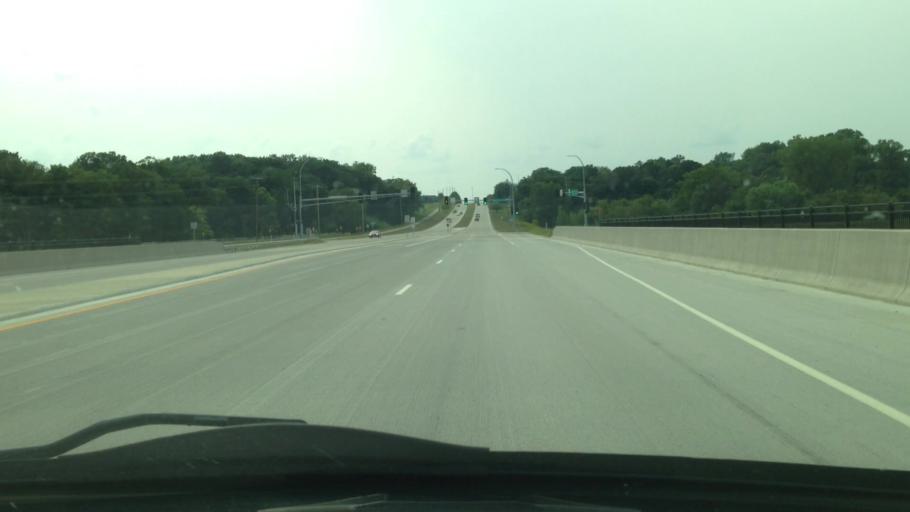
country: US
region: Minnesota
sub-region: Olmsted County
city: Rochester
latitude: 44.0796
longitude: -92.4710
